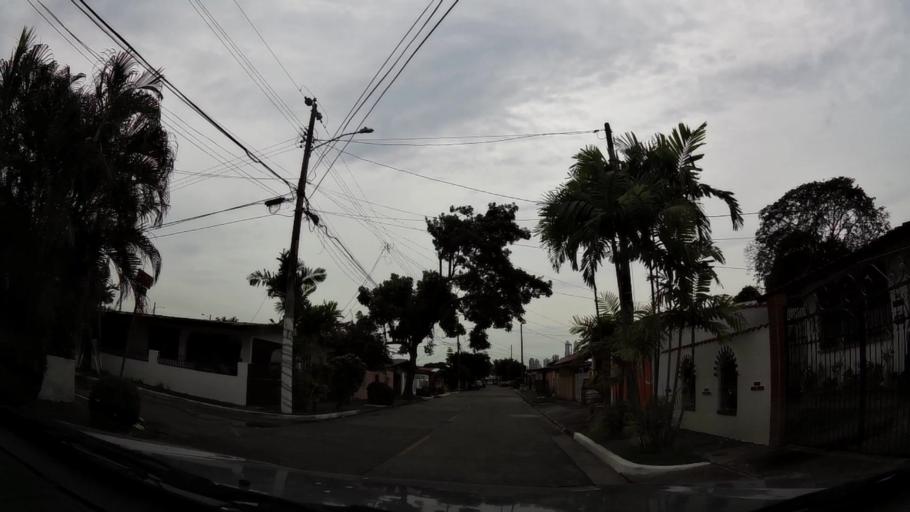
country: PA
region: Panama
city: San Miguelito
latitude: 9.0353
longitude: -79.4765
